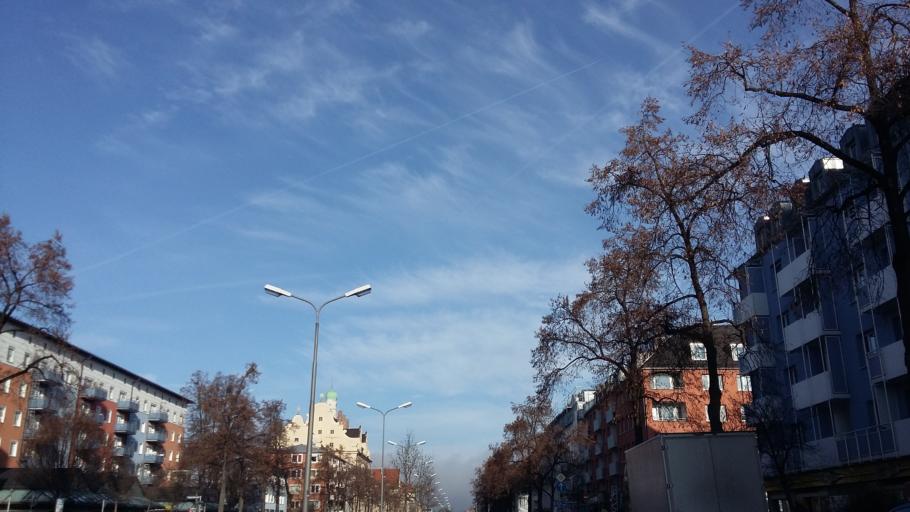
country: DE
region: Bavaria
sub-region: Upper Bavaria
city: Pasing
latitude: 48.1368
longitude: 11.5032
